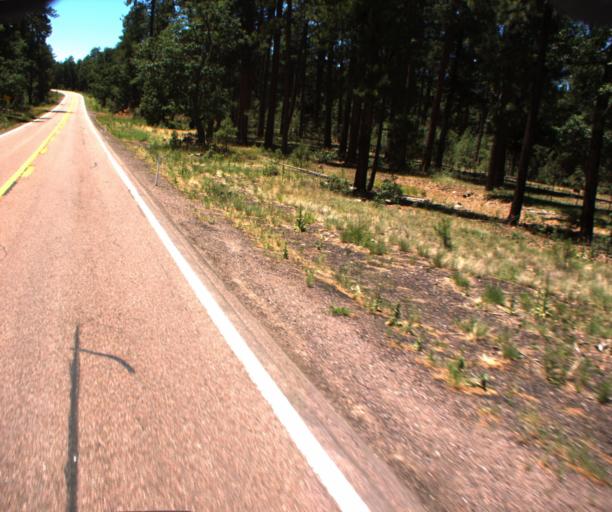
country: US
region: Arizona
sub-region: Gila County
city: Pine
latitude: 34.4557
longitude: -111.4123
